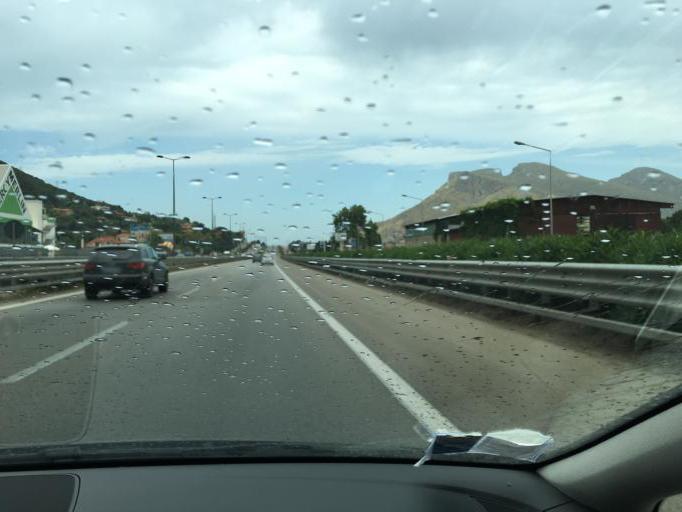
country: IT
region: Sicily
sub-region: Palermo
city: Isola delle Femmine
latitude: 38.1776
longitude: 13.2944
